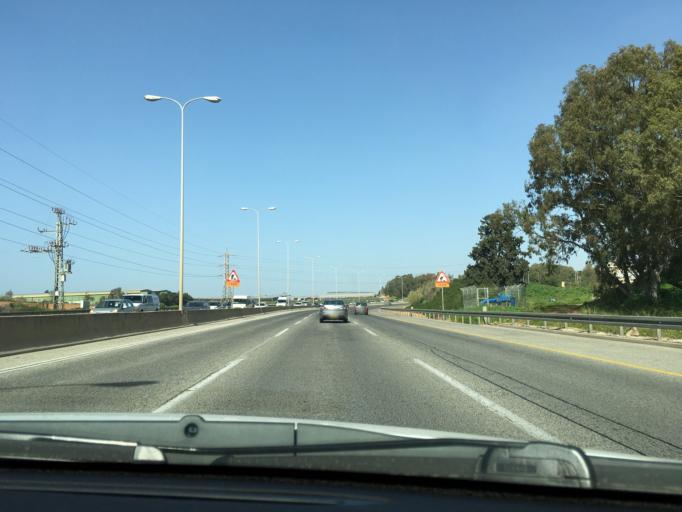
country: IL
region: Central District
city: Hod HaSharon
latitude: 32.1525
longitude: 34.8727
